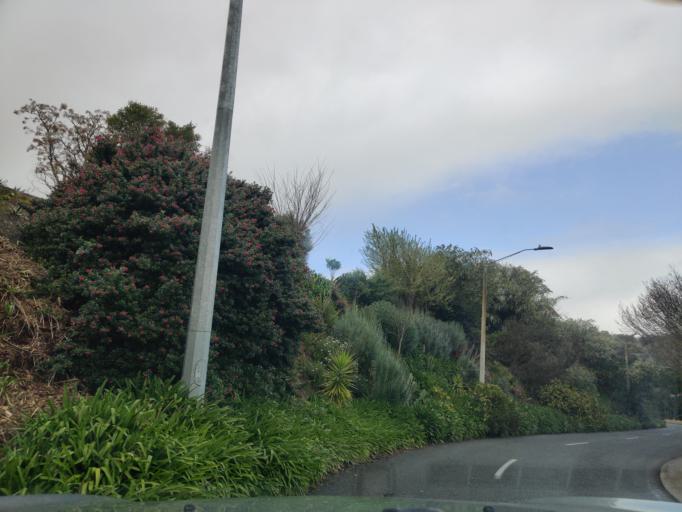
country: NZ
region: Hawke's Bay
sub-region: Hastings District
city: Hastings
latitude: -39.6738
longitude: 176.8946
